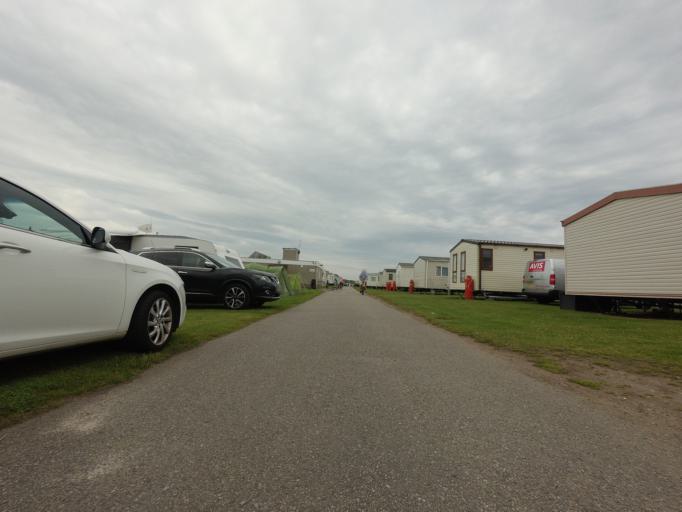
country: GB
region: Scotland
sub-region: Aberdeenshire
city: Banff
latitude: 57.6705
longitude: -2.5539
